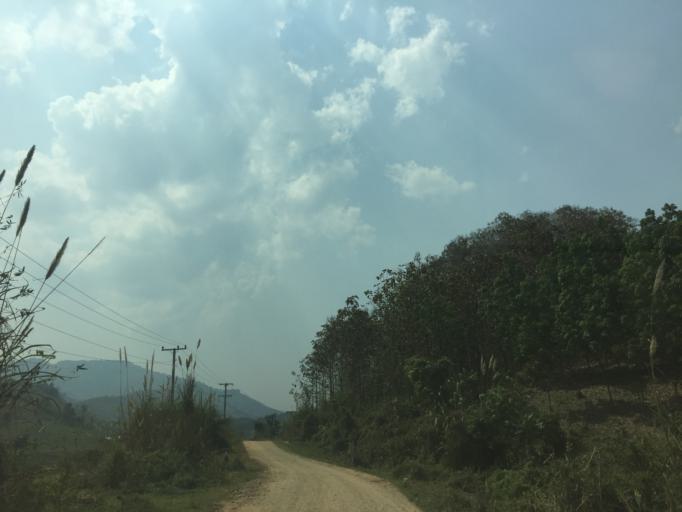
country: TH
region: Nan
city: Thung Chang
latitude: 19.7291
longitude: 100.7437
